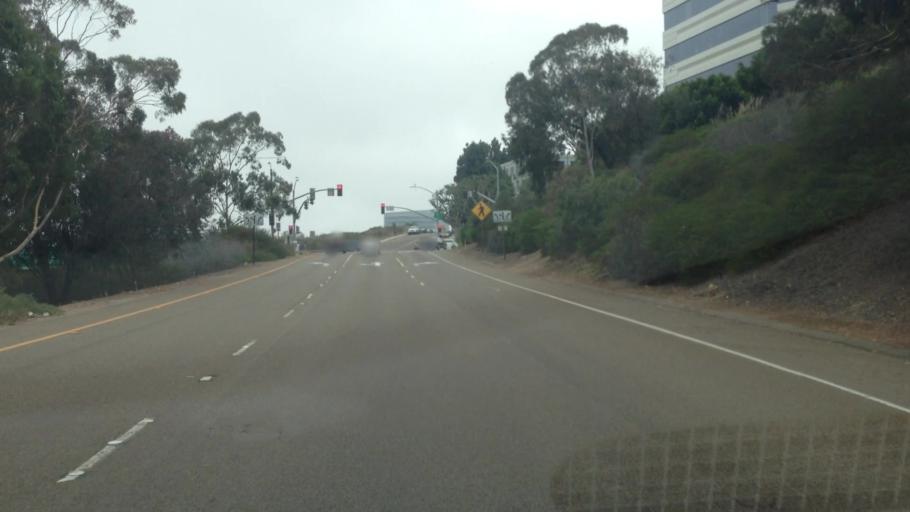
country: US
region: California
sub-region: San Diego County
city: La Jolla
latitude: 32.8672
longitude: -117.2292
